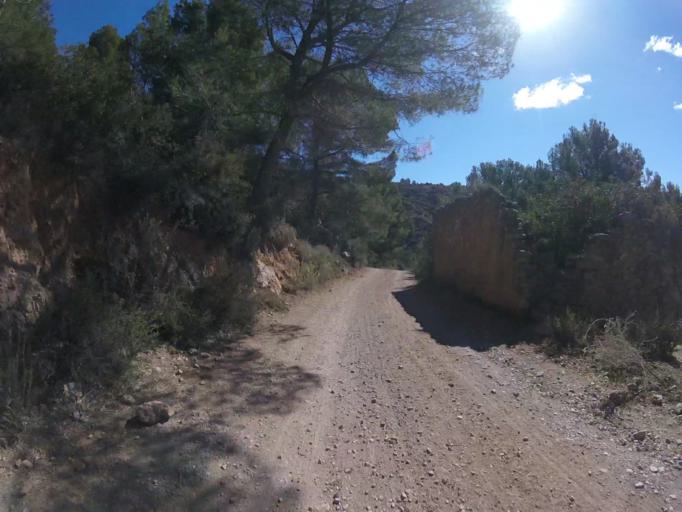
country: ES
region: Valencia
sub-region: Provincia de Castello
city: Benicassim
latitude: 40.0734
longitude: 0.0780
